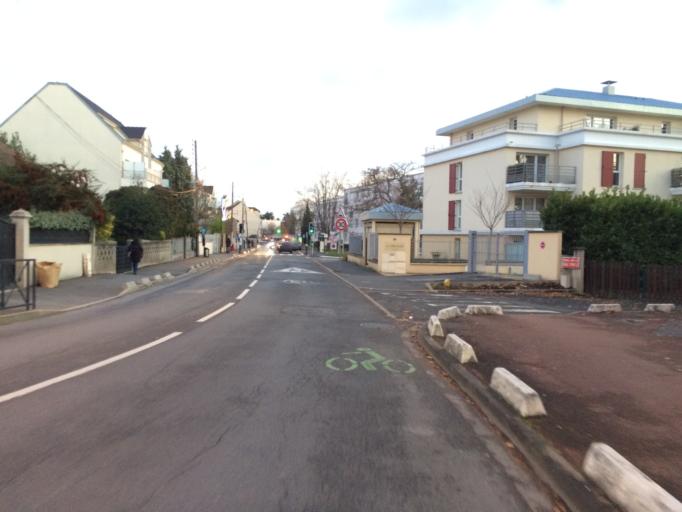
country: FR
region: Ile-de-France
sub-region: Departement de l'Essonne
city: Longjumeau
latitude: 48.6961
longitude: 2.3068
